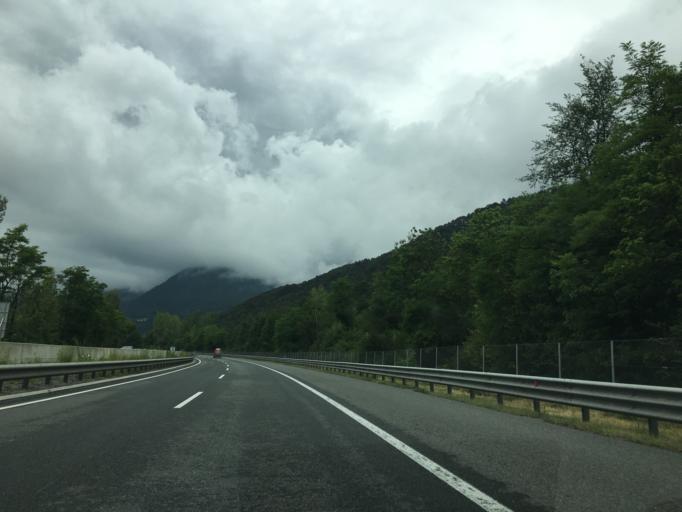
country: AT
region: Tyrol
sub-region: Politischer Bezirk Innsbruck Land
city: Pettnau
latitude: 47.3095
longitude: 11.1186
